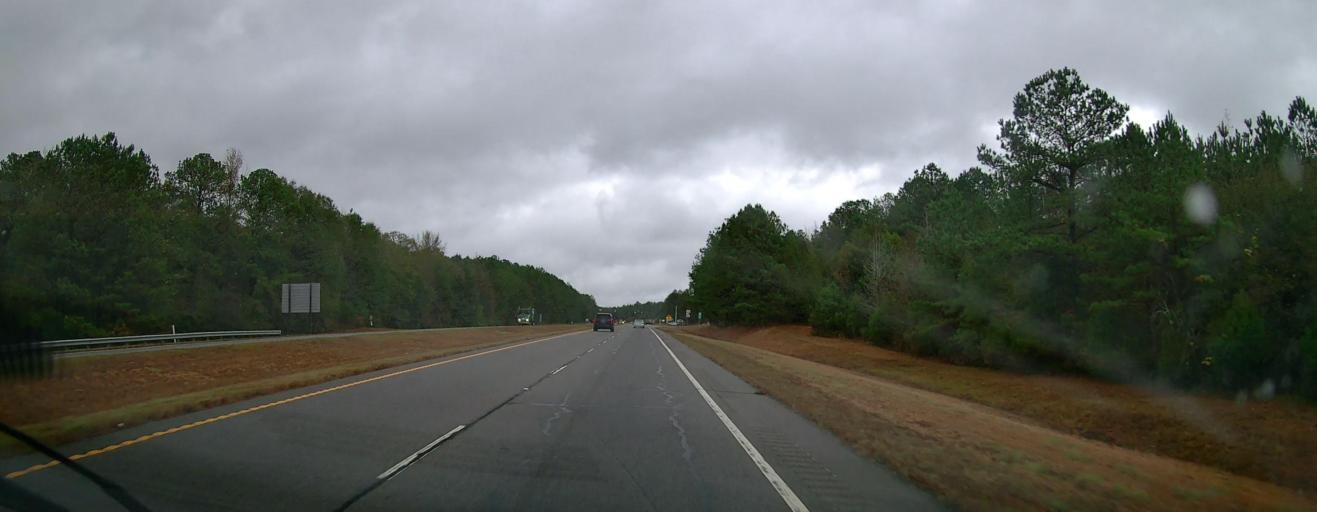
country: US
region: Georgia
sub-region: Oconee County
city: Watkinsville
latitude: 33.8769
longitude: -83.4176
